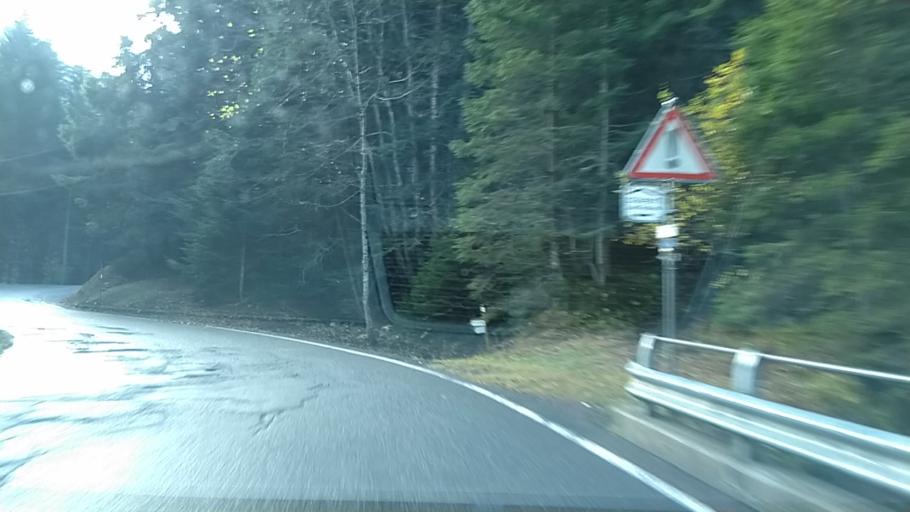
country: CH
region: Valais
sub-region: Monthey District
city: Tanay
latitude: 46.3133
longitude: 6.8498
